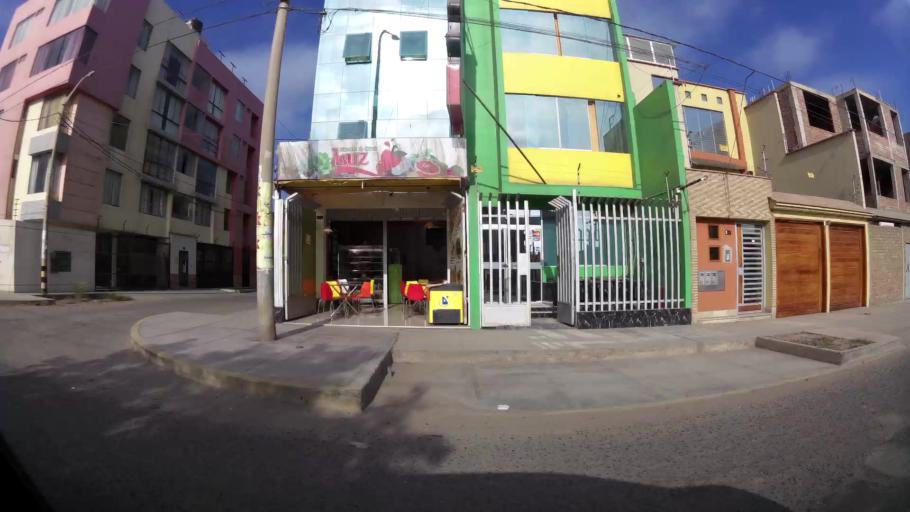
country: PE
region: La Libertad
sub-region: Provincia de Trujillo
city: La Esperanza
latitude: -8.0940
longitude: -79.0481
